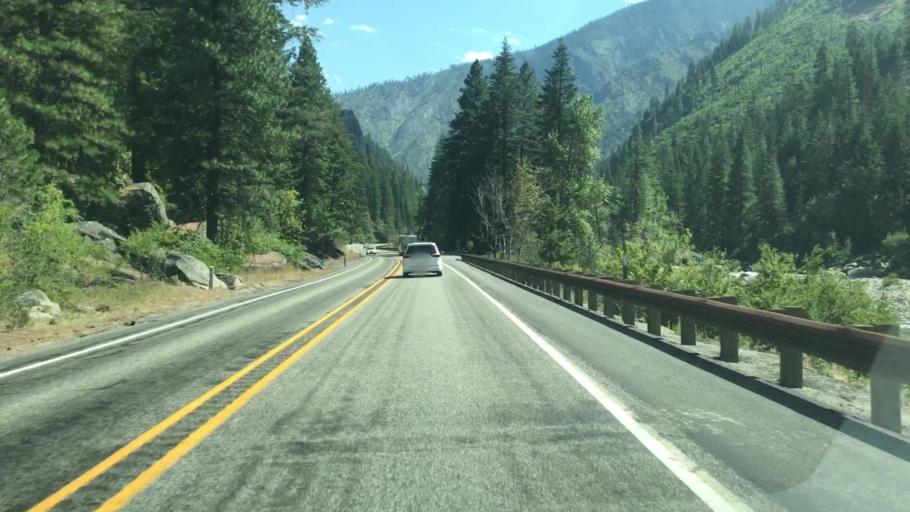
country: US
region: Washington
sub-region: Chelan County
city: Leavenworth
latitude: 47.6100
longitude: -120.7182
